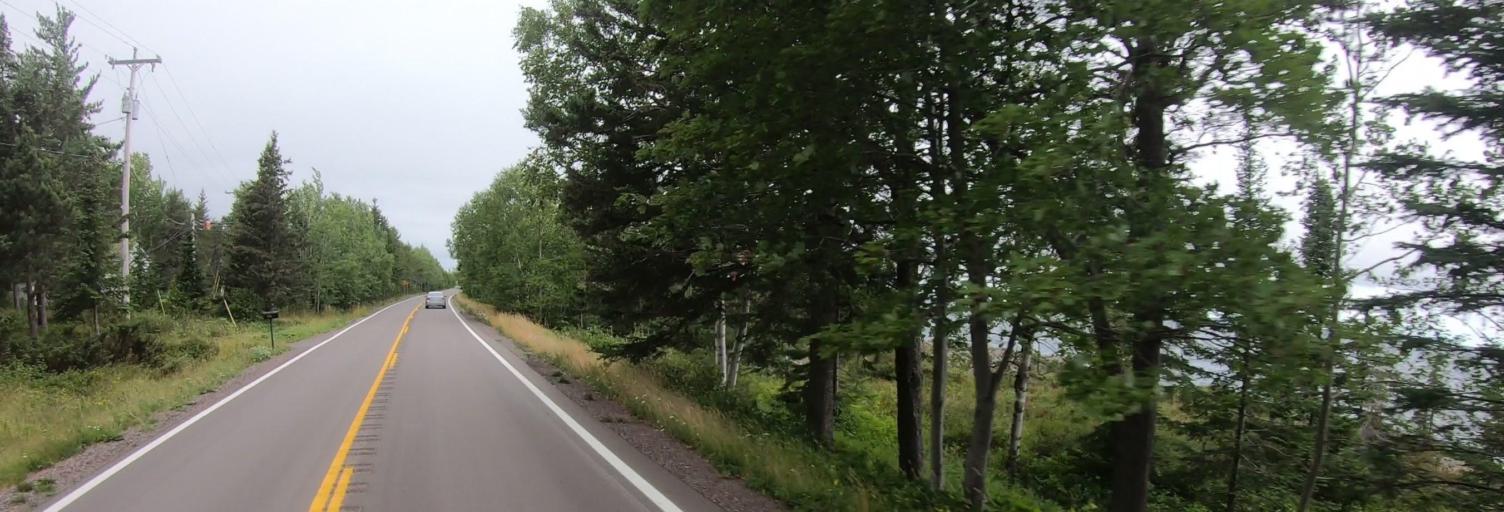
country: US
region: Michigan
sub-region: Keweenaw County
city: Eagle River
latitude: 47.4767
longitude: -88.0198
